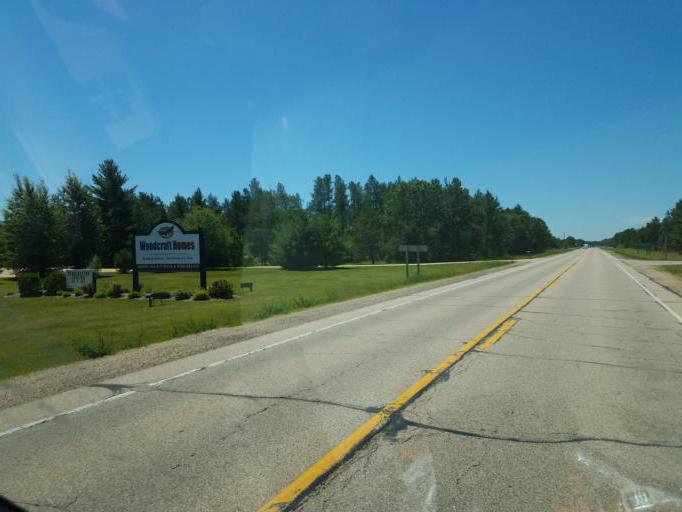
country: US
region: Wisconsin
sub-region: Juneau County
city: New Lisbon
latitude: 44.0416
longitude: -90.0286
